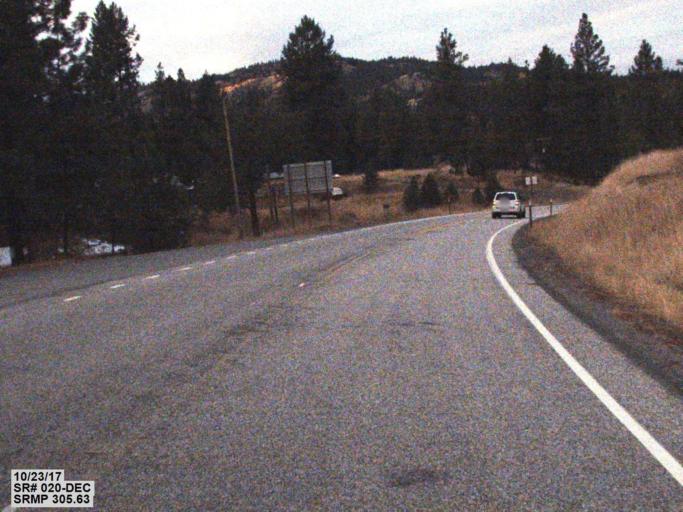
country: US
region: Washington
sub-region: Ferry County
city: Republic
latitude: 48.6455
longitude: -118.6857
